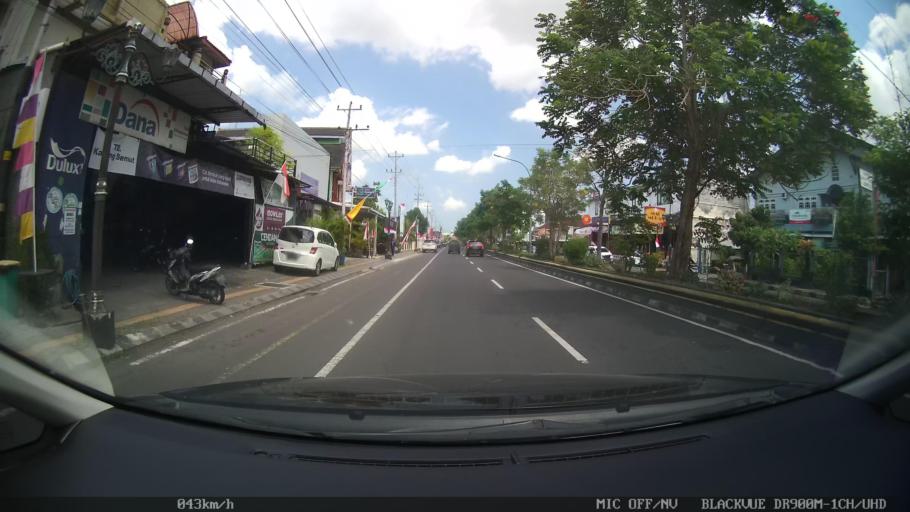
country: ID
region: Daerah Istimewa Yogyakarta
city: Bantul
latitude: -7.8824
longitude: 110.3323
